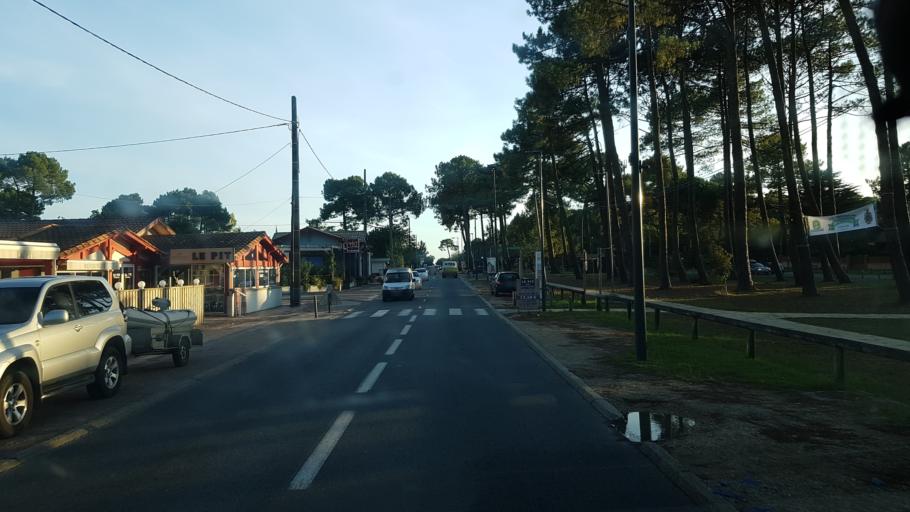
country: FR
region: Aquitaine
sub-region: Departement de la Gironde
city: Ares
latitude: 44.7492
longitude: -1.1809
